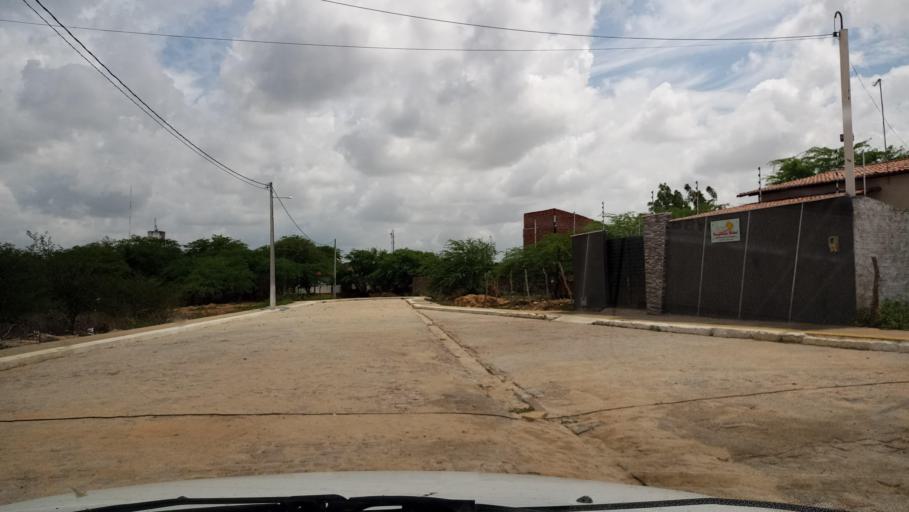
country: BR
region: Rio Grande do Norte
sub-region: Tangara
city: Tangara
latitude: -6.1099
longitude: -35.7153
